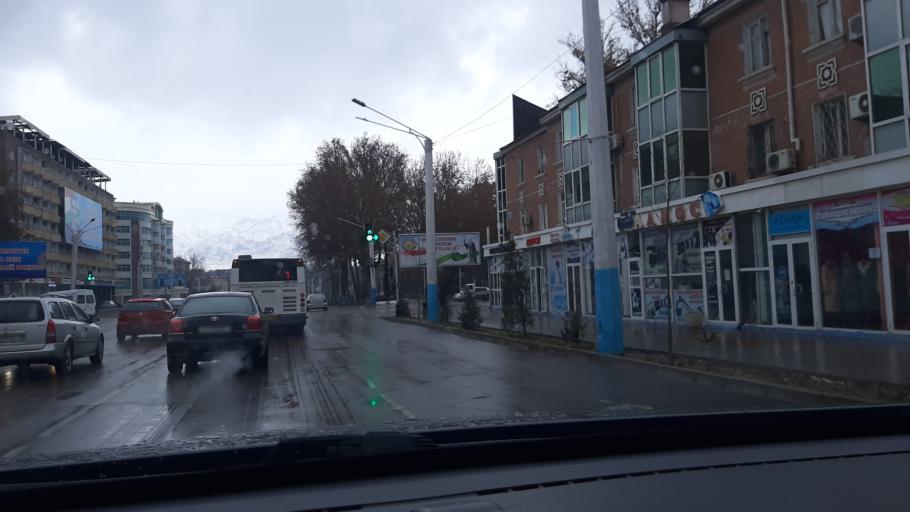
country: TJ
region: Viloyati Sughd
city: Khujand
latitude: 40.2813
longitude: 69.6252
